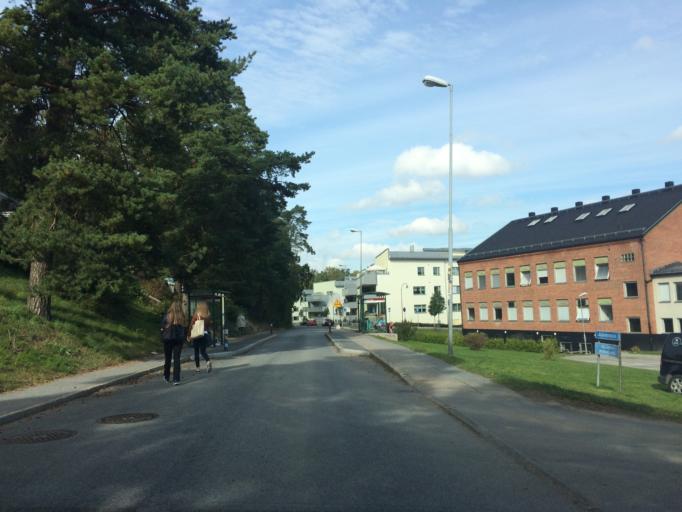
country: SE
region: Stockholm
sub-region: Sollentuna Kommun
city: Sollentuna
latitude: 59.4477
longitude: 17.9346
